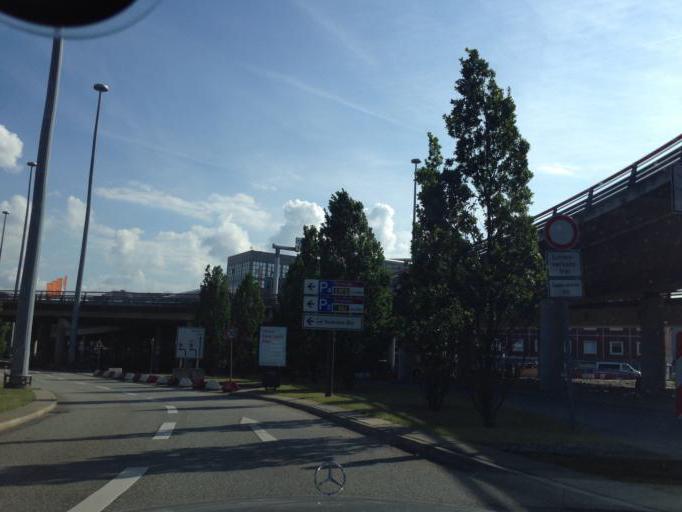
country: DE
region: Hamburg
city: Fuhlsbuettel
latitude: 53.6346
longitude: 10.0067
